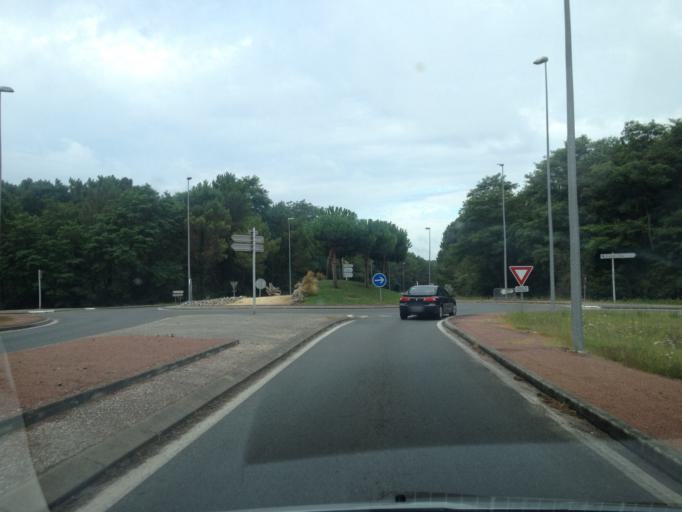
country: FR
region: Poitou-Charentes
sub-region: Departement de la Charente-Maritime
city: Saint-Palais-sur-Mer
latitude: 45.6575
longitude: -1.0888
